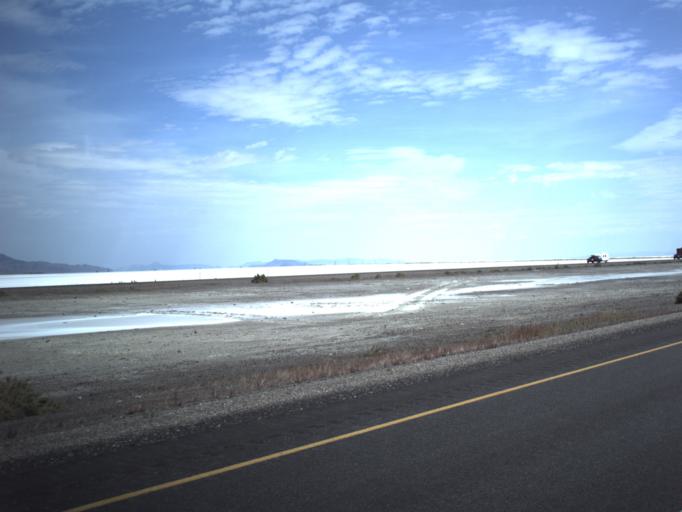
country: US
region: Utah
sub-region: Tooele County
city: Wendover
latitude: 40.7398
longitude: -113.9175
